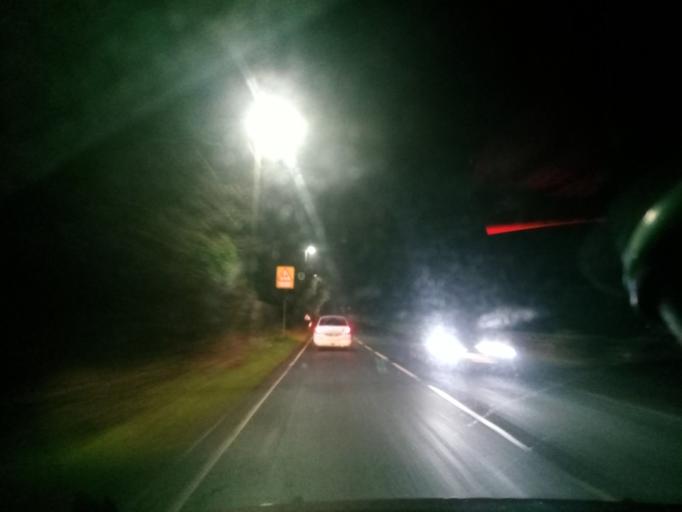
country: GB
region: England
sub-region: Northumberland
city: Meldon
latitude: 55.1032
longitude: -1.8422
